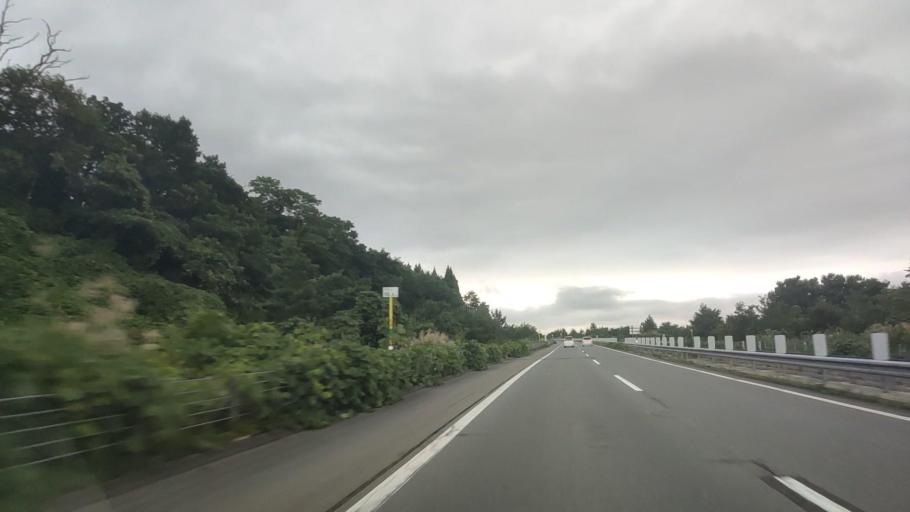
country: JP
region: Hokkaido
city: Nanae
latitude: 41.9067
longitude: 140.6969
